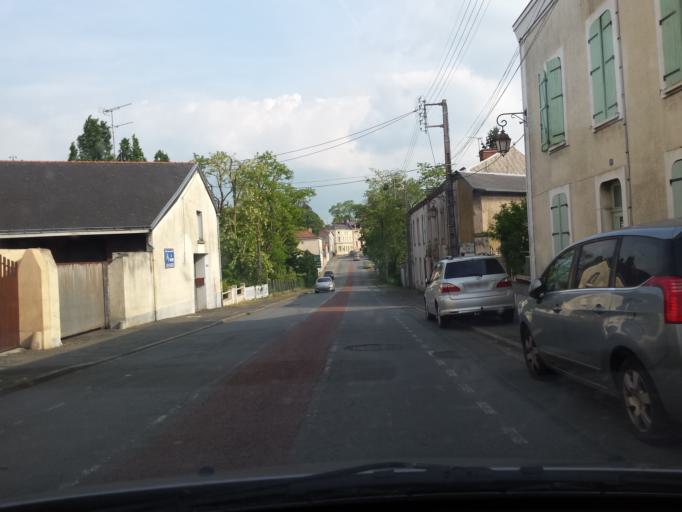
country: FR
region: Pays de la Loire
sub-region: Departement de Maine-et-Loire
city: Chemille-Melay
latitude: 47.2073
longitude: -0.7293
